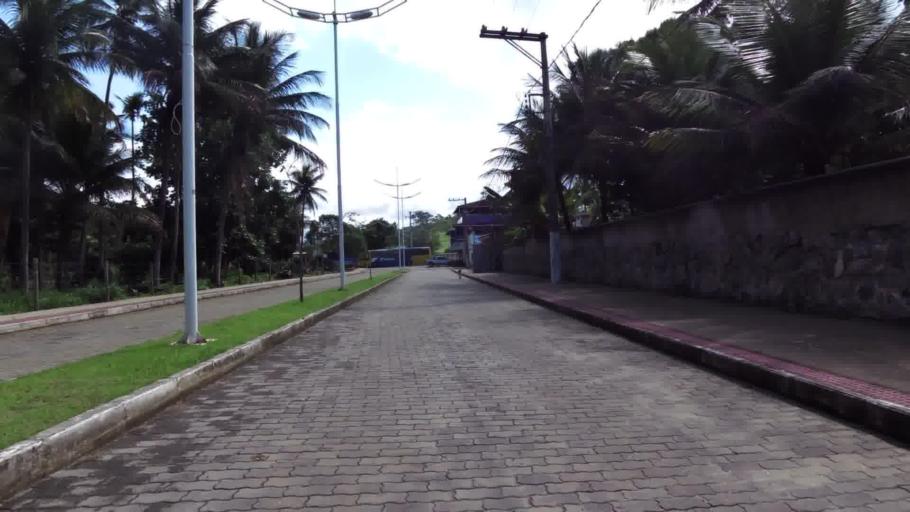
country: BR
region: Espirito Santo
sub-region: Piuma
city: Piuma
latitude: -20.8222
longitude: -40.6839
